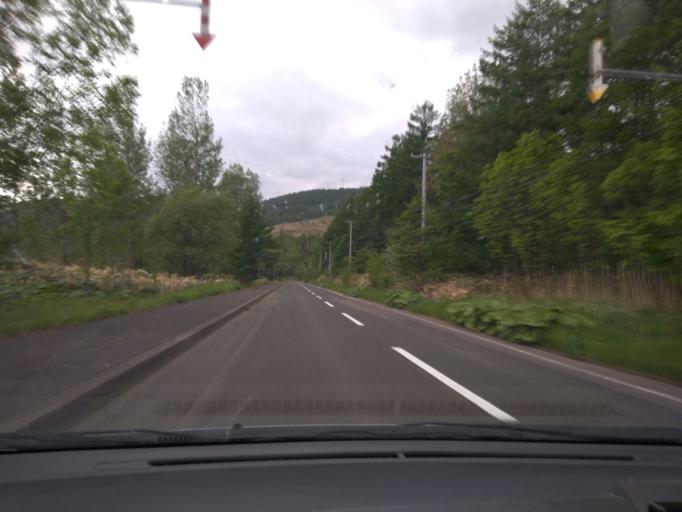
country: JP
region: Hokkaido
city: Shimo-furano
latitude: 43.1737
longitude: 142.5178
